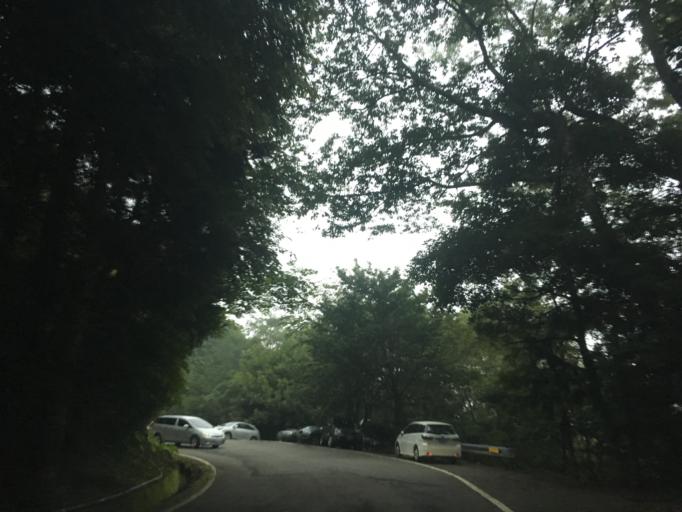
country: TW
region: Taiwan
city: Fengyuan
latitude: 24.2438
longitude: 120.9343
